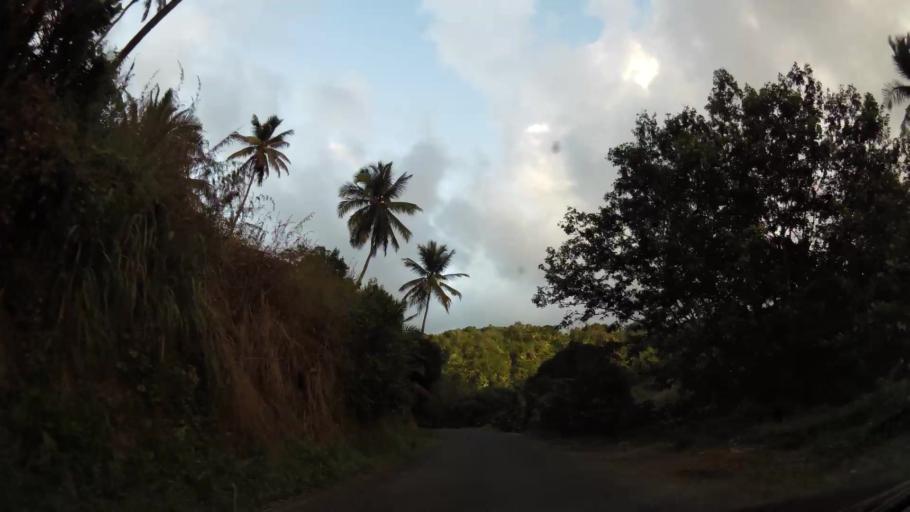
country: DM
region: Saint Andrew
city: Calibishie
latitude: 15.5875
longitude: -61.4024
